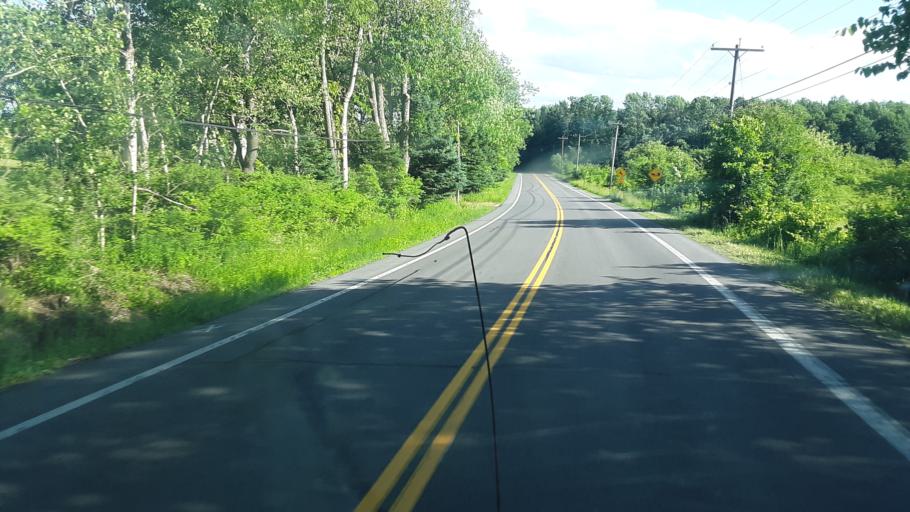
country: US
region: New York
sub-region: Oneida County
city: Rome
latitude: 43.3273
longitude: -75.4771
